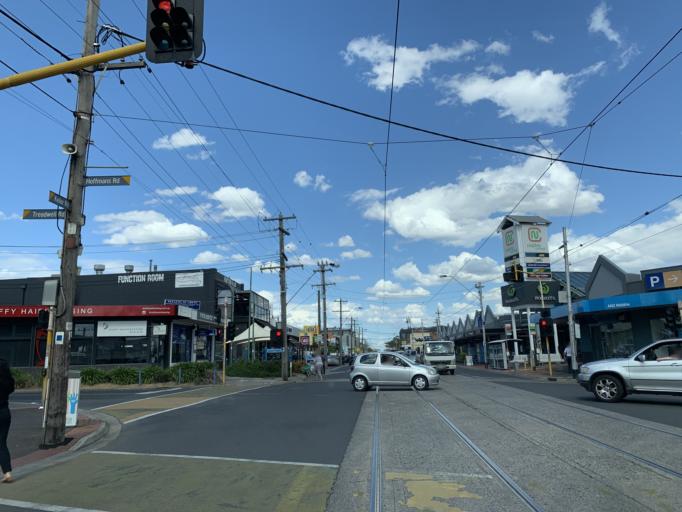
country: AU
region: Victoria
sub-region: Moonee Valley
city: Niddrie
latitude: -37.7373
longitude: 144.8923
